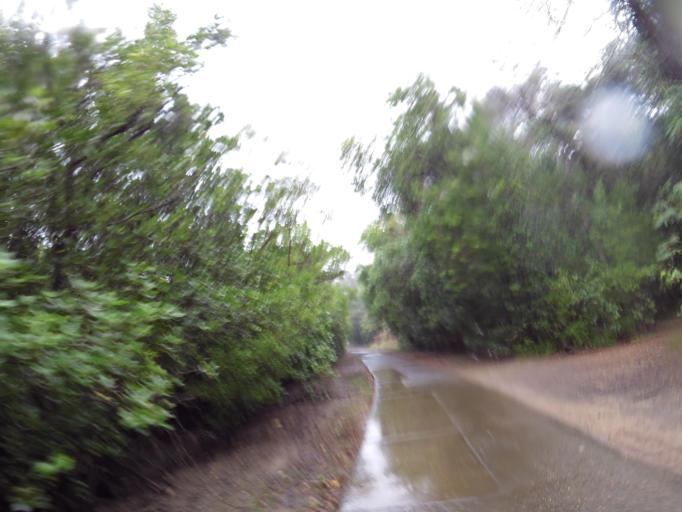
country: AU
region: Queensland
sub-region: Cairns
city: Cairns
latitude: -16.8973
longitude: 145.7534
